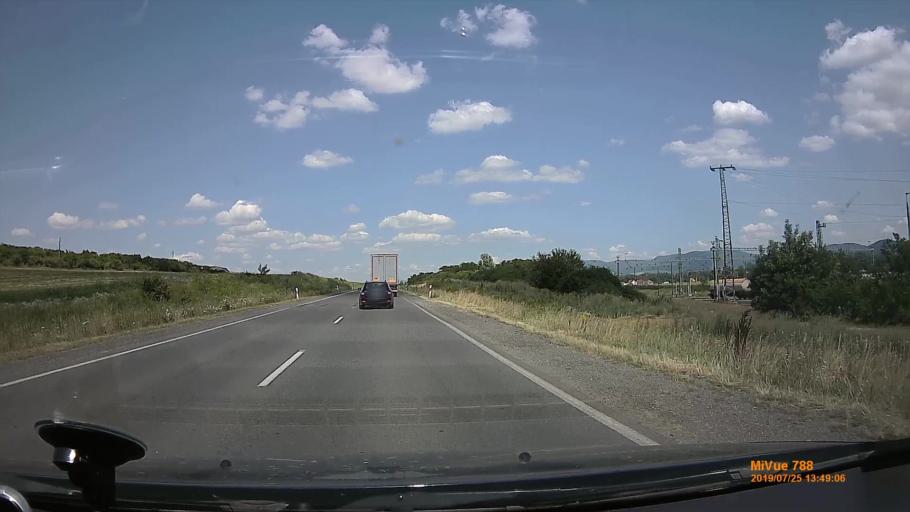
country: HU
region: Borsod-Abauj-Zemplen
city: Gonc
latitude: 48.5127
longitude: 21.2313
